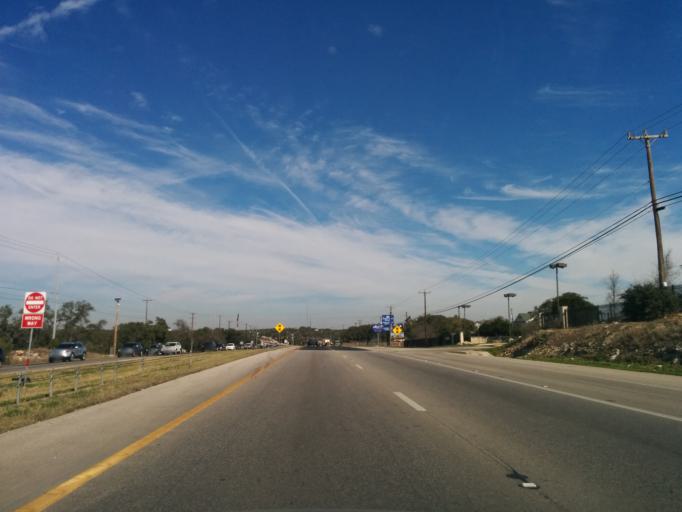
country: US
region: Texas
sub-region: Bexar County
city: Timberwood Park
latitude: 29.6634
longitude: -98.4500
